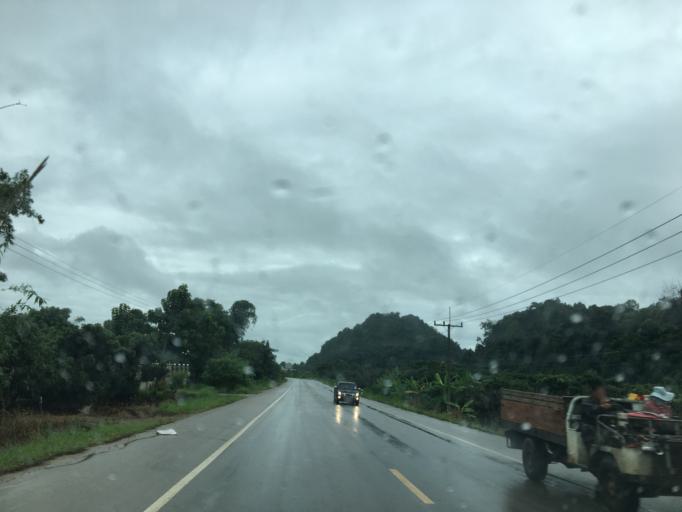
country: TH
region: Chiang Rai
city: Pa Daet
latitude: 19.5786
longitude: 99.9920
